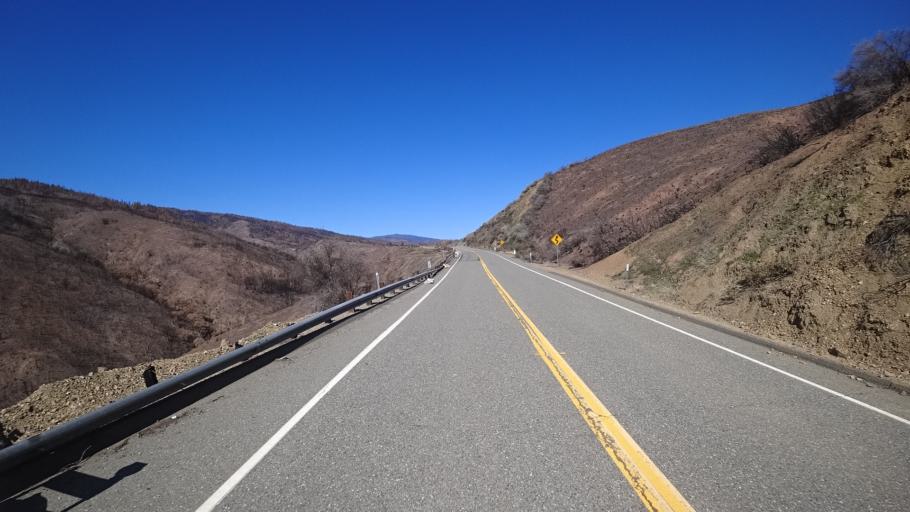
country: US
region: California
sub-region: Tehama County
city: Rancho Tehama Reserve
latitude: 39.6637
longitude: -122.6626
